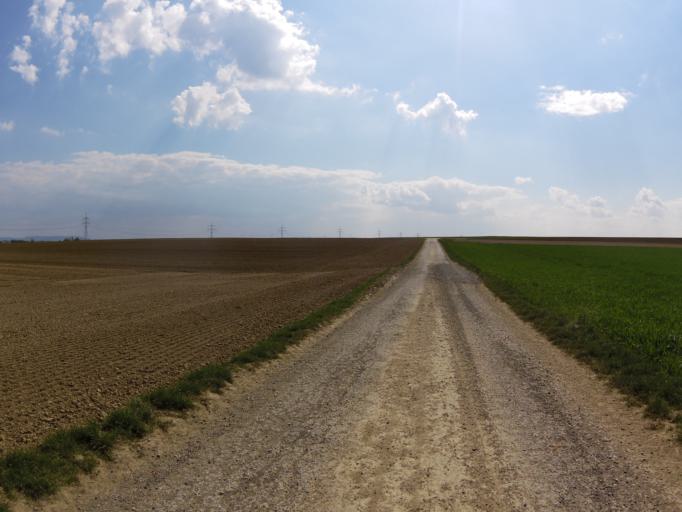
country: DE
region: Bavaria
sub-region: Regierungsbezirk Unterfranken
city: Oberpleichfeld
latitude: 49.8427
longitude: 10.0794
